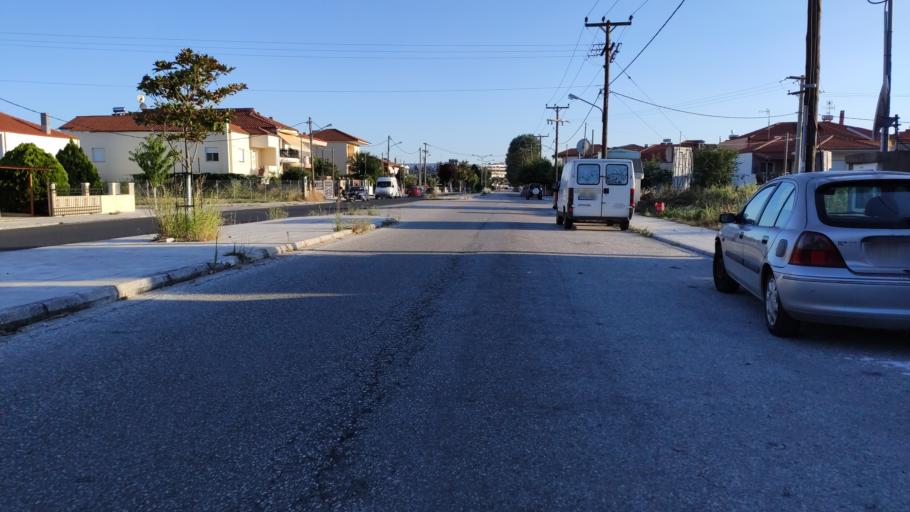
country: GR
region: East Macedonia and Thrace
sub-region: Nomos Rodopis
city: Komotini
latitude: 41.1303
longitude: 25.3965
